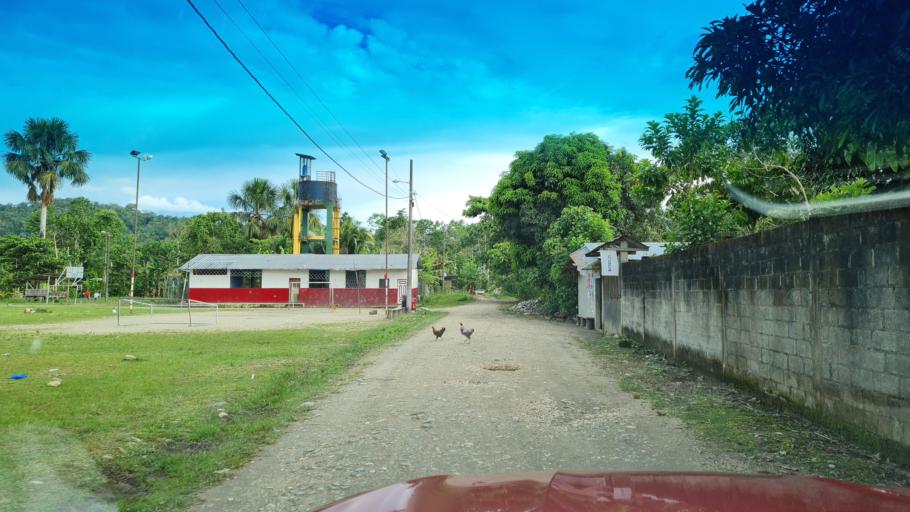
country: EC
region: Napo
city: Tena
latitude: -1.0468
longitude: -77.7618
